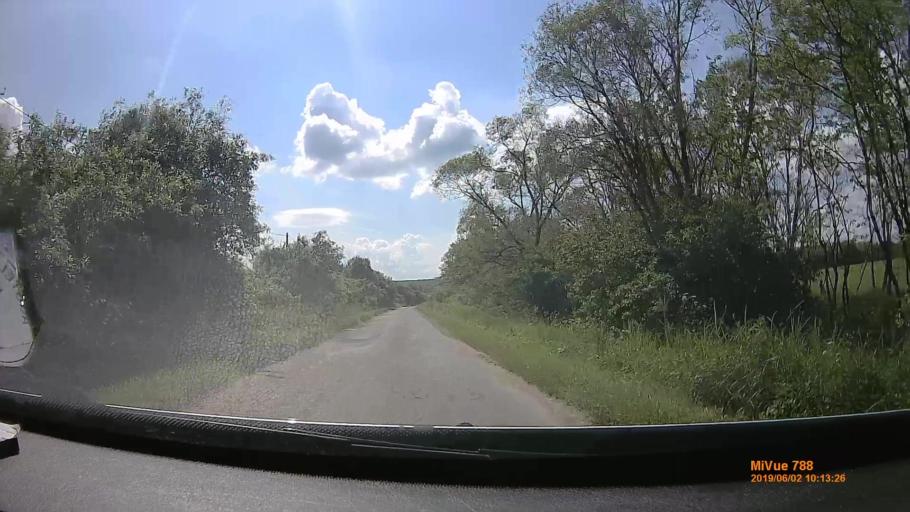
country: HU
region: Borsod-Abauj-Zemplen
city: Szendro
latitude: 48.5149
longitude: 20.7850
